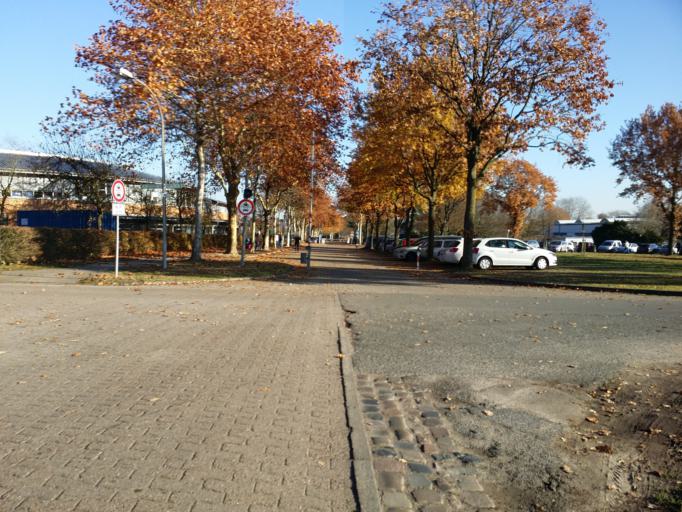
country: DE
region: Lower Saxony
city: Oyten
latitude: 53.0721
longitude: 9.0098
